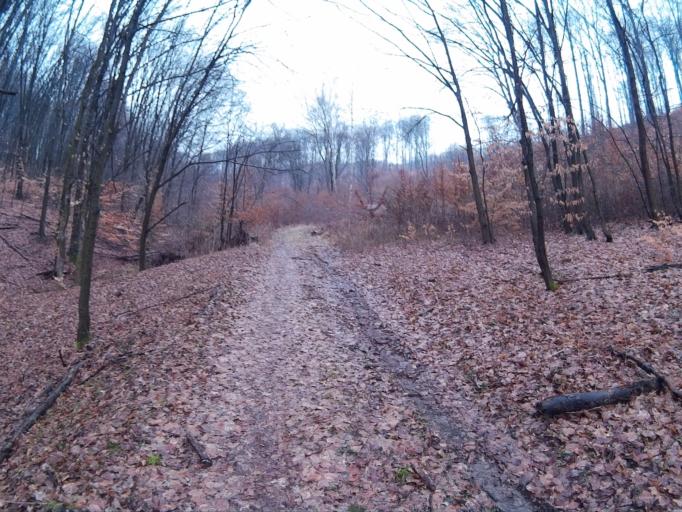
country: HU
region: Borsod-Abauj-Zemplen
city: Sarospatak
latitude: 48.4202
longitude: 21.5545
